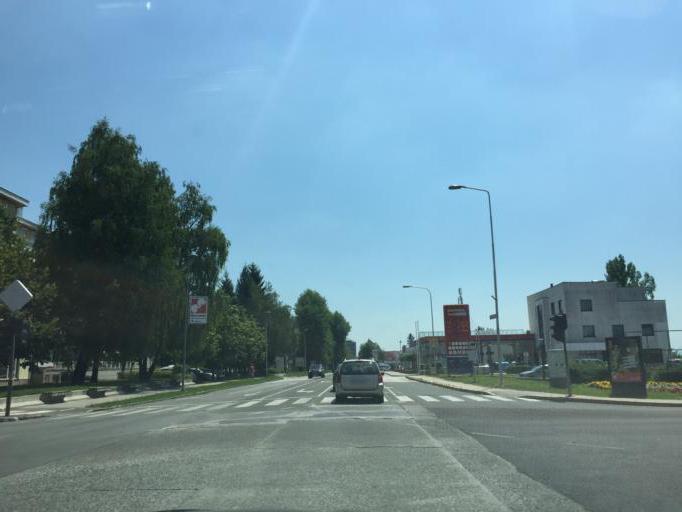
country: SI
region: Kranj
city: Kranj
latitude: 46.2482
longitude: 14.3491
